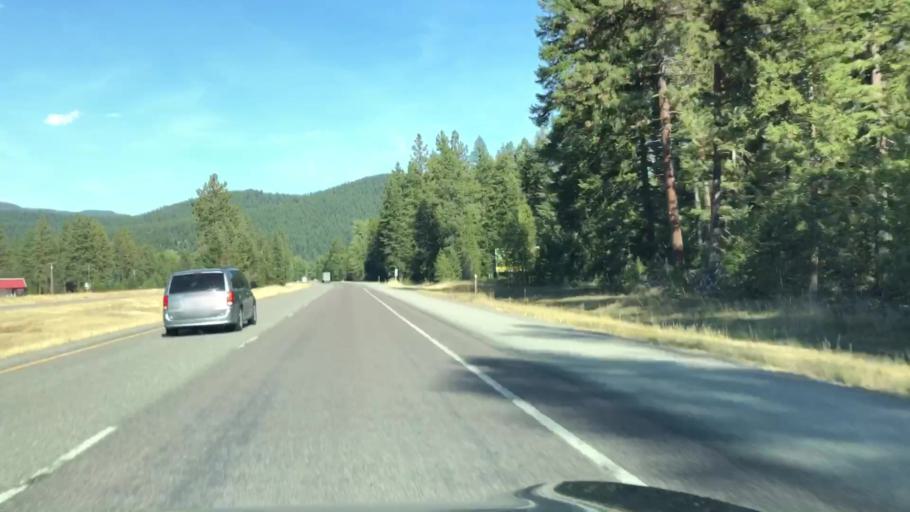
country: US
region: Montana
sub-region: Sanders County
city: Thompson Falls
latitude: 47.3767
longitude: -115.3695
